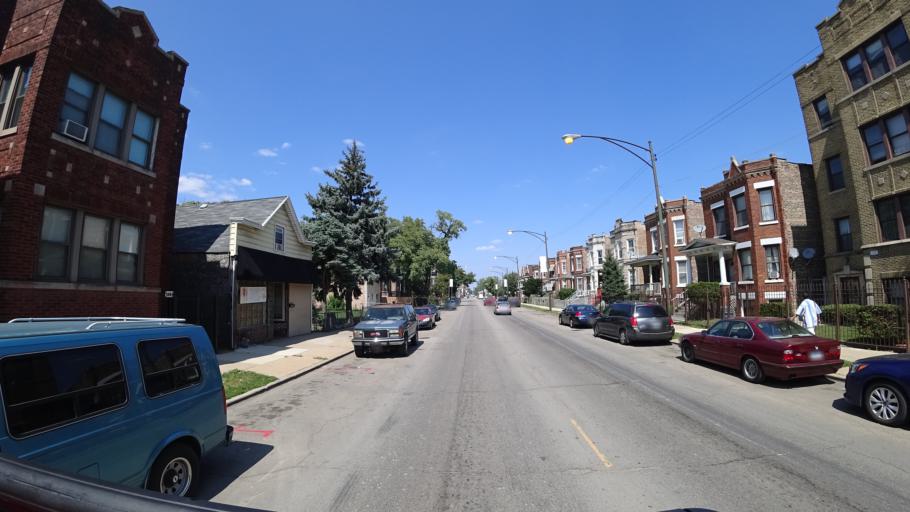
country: US
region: Illinois
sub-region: Cook County
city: Cicero
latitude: 41.8608
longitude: -87.7348
